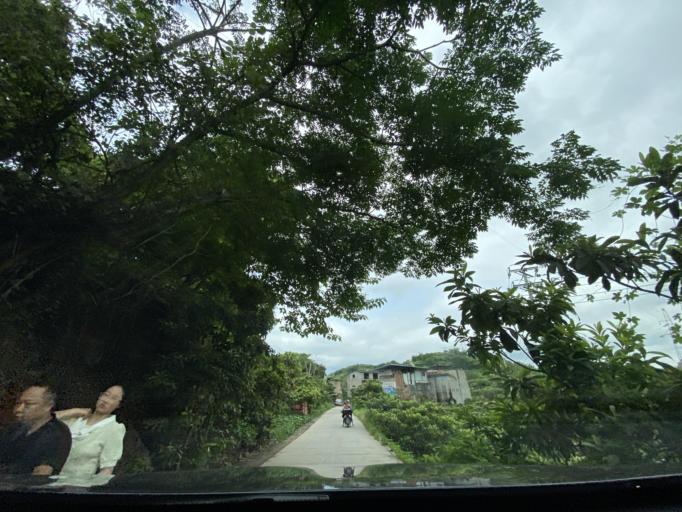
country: CN
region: Sichuan
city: Jiancheng
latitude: 30.3985
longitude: 104.5600
